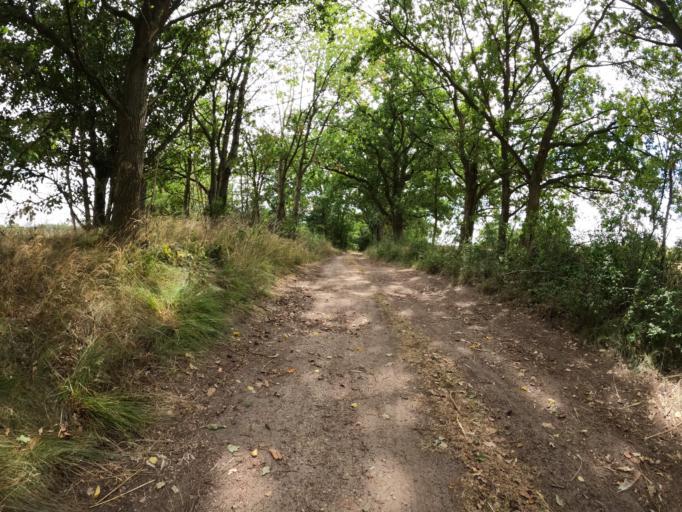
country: DE
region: Mecklenburg-Vorpommern
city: Loitz
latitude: 53.3807
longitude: 13.4470
